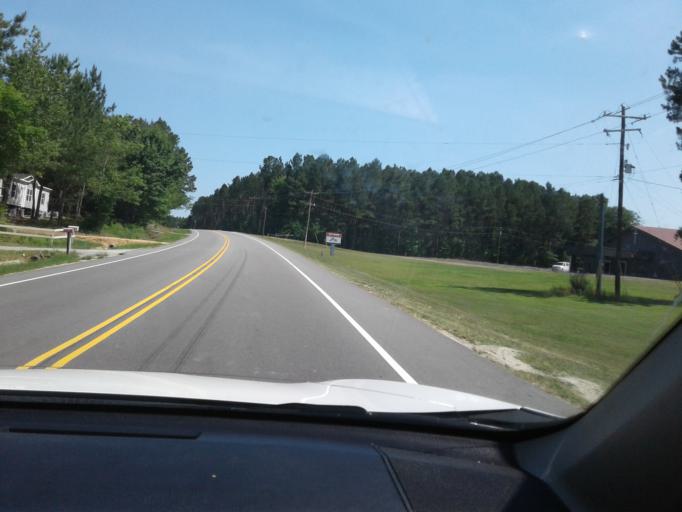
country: US
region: North Carolina
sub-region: Harnett County
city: Lillington
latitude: 35.4410
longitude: -78.8276
